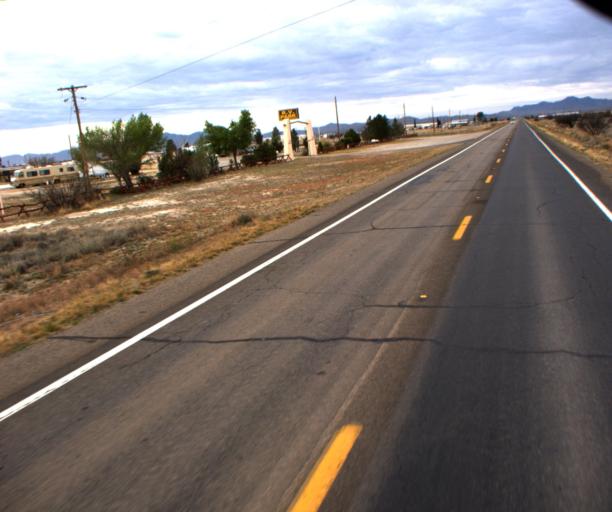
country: US
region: Arizona
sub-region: Cochise County
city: Willcox
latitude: 32.2309
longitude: -109.8584
